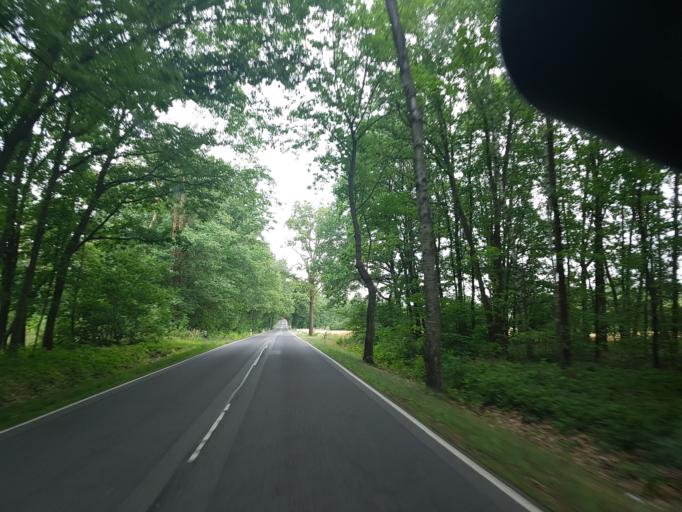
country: DE
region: Brandenburg
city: Lebusa
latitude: 51.8100
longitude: 13.4212
